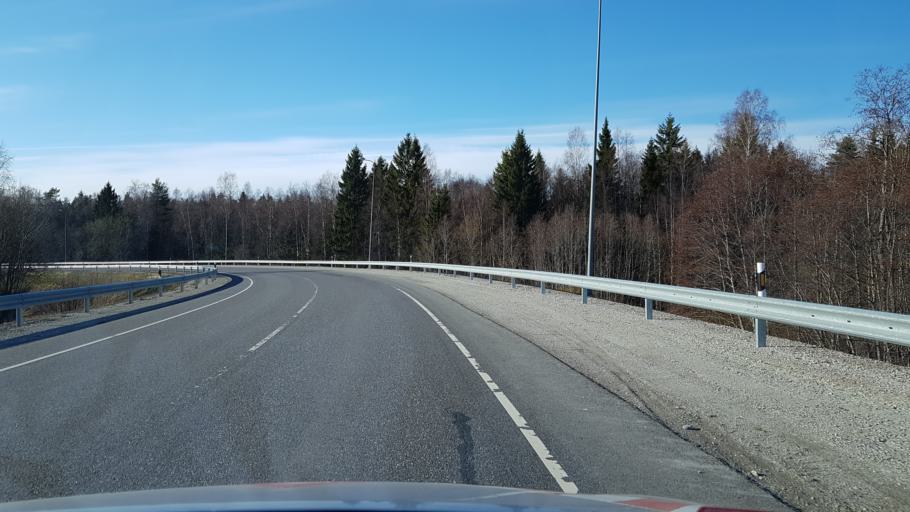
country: EE
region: Laeaene-Virumaa
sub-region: Tapa vald
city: Tapa
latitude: 59.4555
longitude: 25.9422
